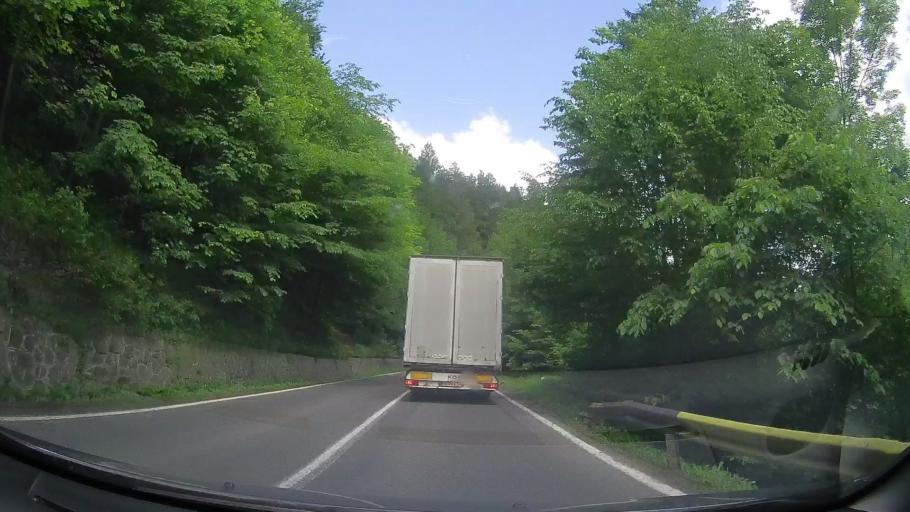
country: RO
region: Prahova
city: Maneciu
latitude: 45.3677
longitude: 25.9301
